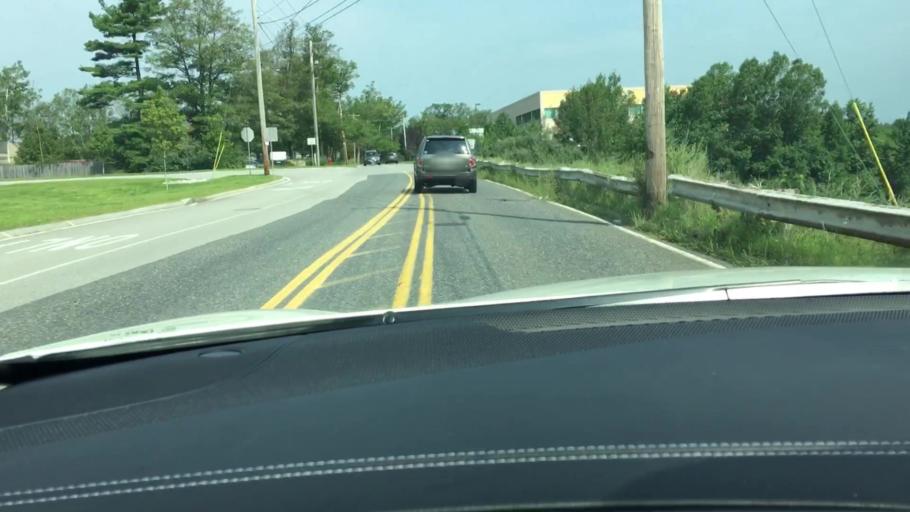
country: US
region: Massachusetts
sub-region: Worcester County
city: Northborough
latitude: 42.2857
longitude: -71.6550
